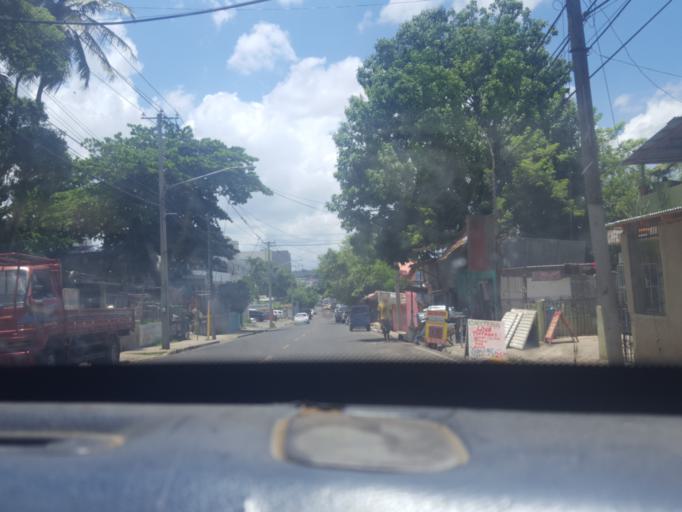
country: DO
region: Santiago
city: Santiago de los Caballeros
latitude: 19.4730
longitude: -70.7166
